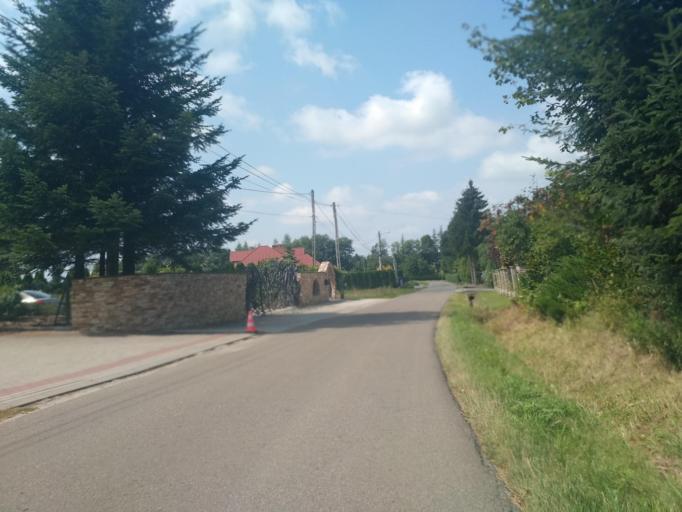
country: PL
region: Subcarpathian Voivodeship
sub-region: Powiat lancucki
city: Kraczkowa
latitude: 50.0348
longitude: 22.1937
